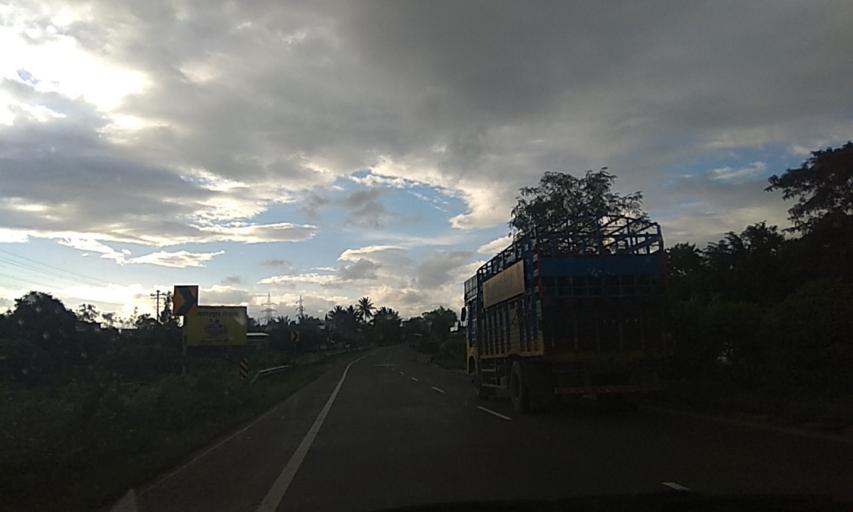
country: IN
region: Maharashtra
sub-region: Satara Division
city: Rahimatpur
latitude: 17.5277
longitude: 74.0674
